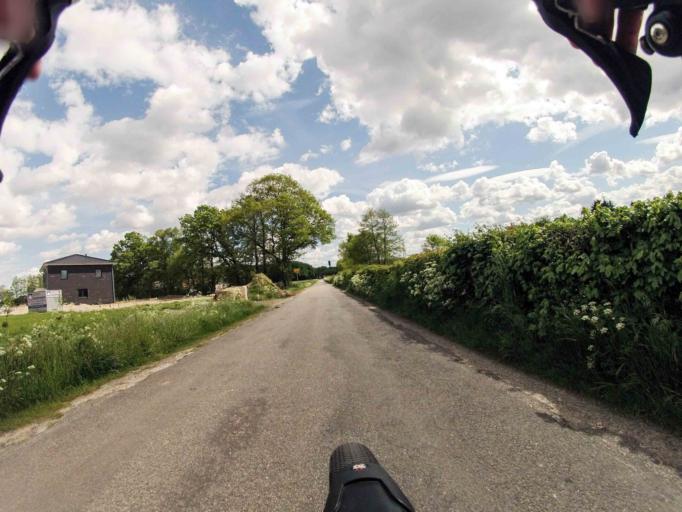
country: DE
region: North Rhine-Westphalia
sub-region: Regierungsbezirk Munster
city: Westerkappeln
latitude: 52.3179
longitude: 7.8910
